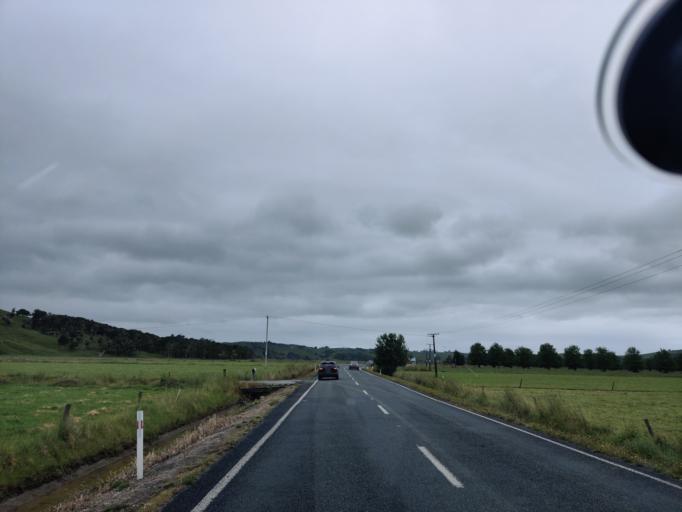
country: NZ
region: Northland
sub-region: Kaipara District
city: Dargaville
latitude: -36.1192
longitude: 174.0816
